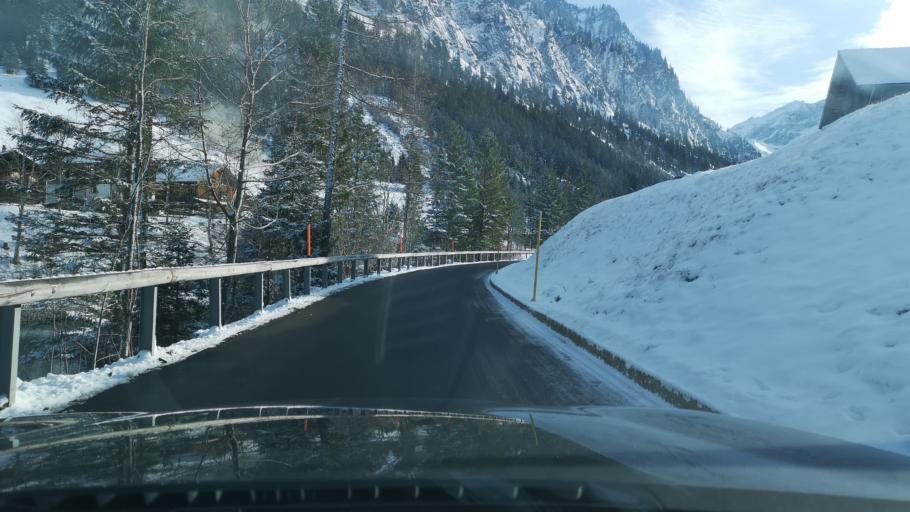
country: LI
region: Triesenberg
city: Triesenberg
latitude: 47.1088
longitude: 9.5763
